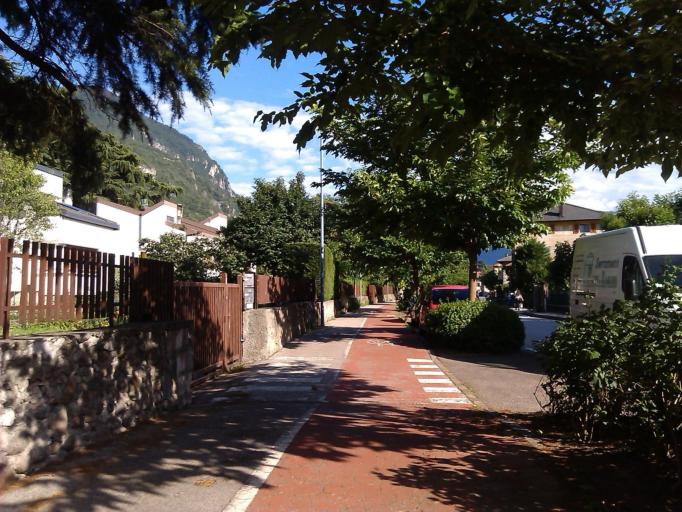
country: IT
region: Trentino-Alto Adige
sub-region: Provincia di Trento
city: Meano
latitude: 46.1124
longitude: 11.1086
